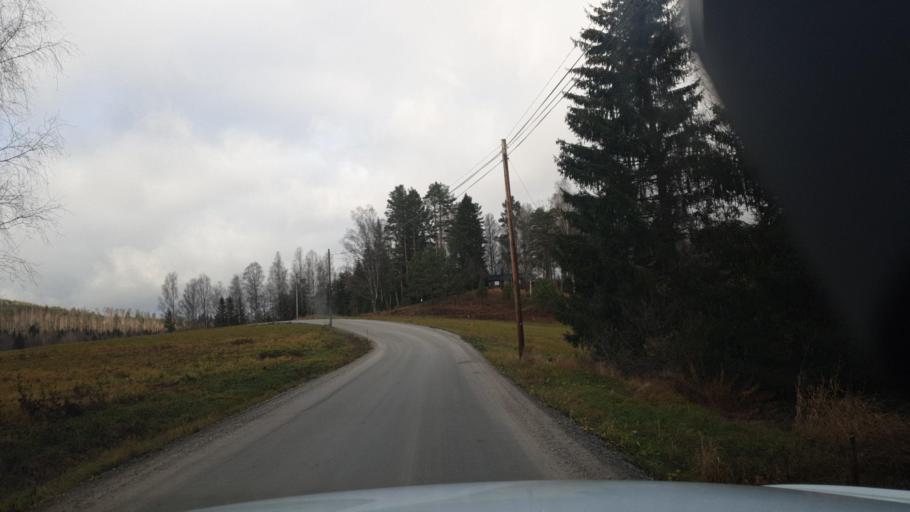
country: SE
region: Vaermland
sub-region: Sunne Kommun
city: Sunne
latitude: 59.6880
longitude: 12.8916
